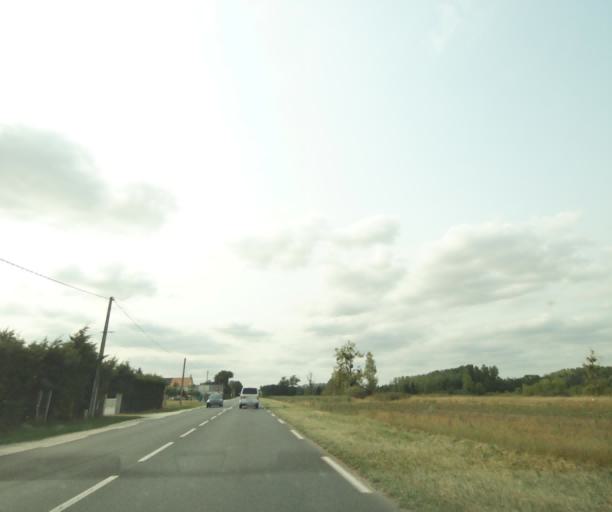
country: FR
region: Centre
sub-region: Departement de l'Indre
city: Chatillon-sur-Indre
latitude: 46.9978
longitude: 1.1544
